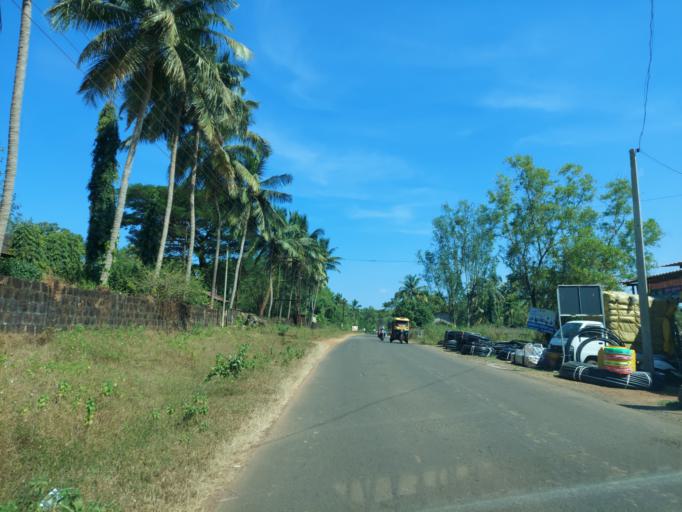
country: IN
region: Maharashtra
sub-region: Sindhudurg
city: Kudal
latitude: 15.9882
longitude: 73.6751
